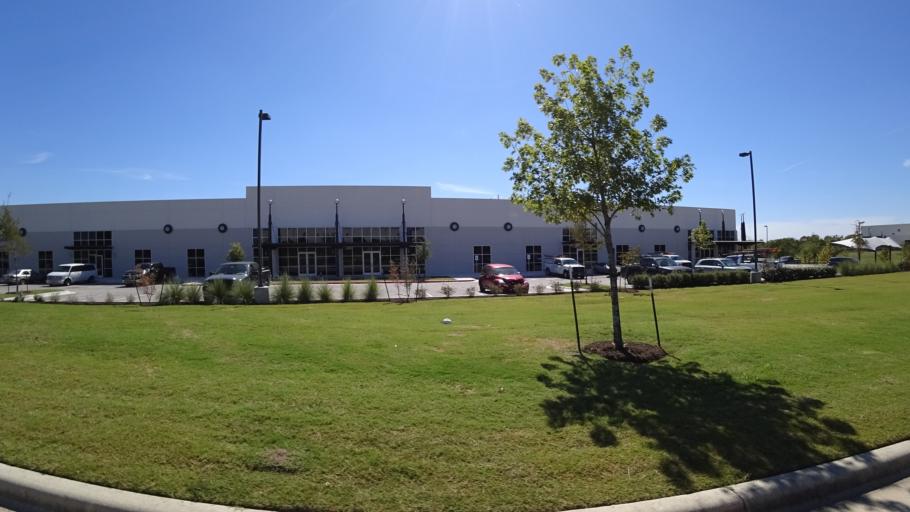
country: US
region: Texas
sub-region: Travis County
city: Austin
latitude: 30.2069
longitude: -97.6956
